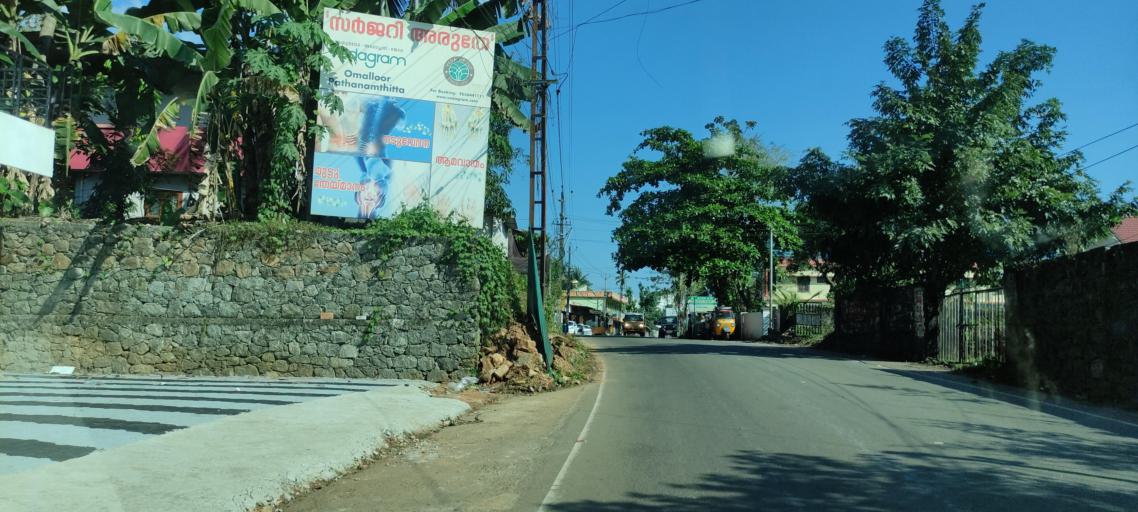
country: IN
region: Kerala
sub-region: Pattanamtitta
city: Pathanamthitta
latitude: 9.2678
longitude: 76.8012
